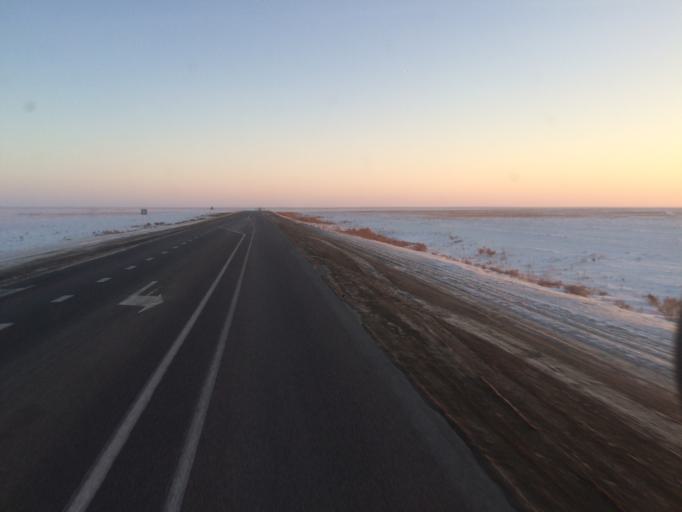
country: KZ
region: Qyzylorda
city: Sekseuil
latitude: 47.6027
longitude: 61.5012
